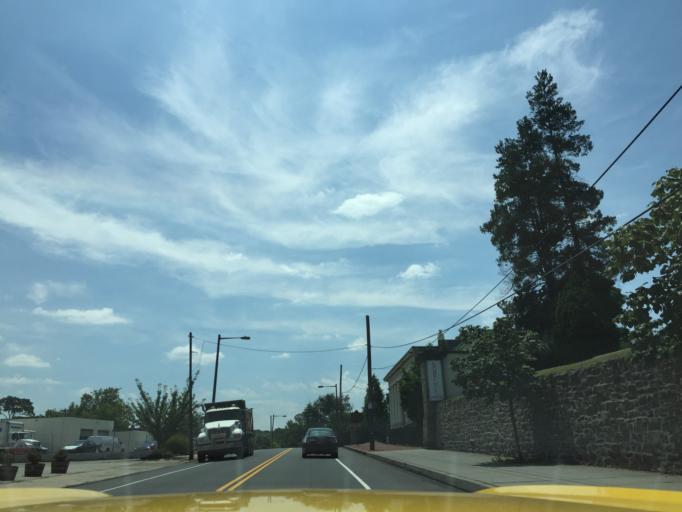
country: US
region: Pennsylvania
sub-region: Montgomery County
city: Bala-Cynwyd
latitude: 40.0049
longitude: -75.1874
